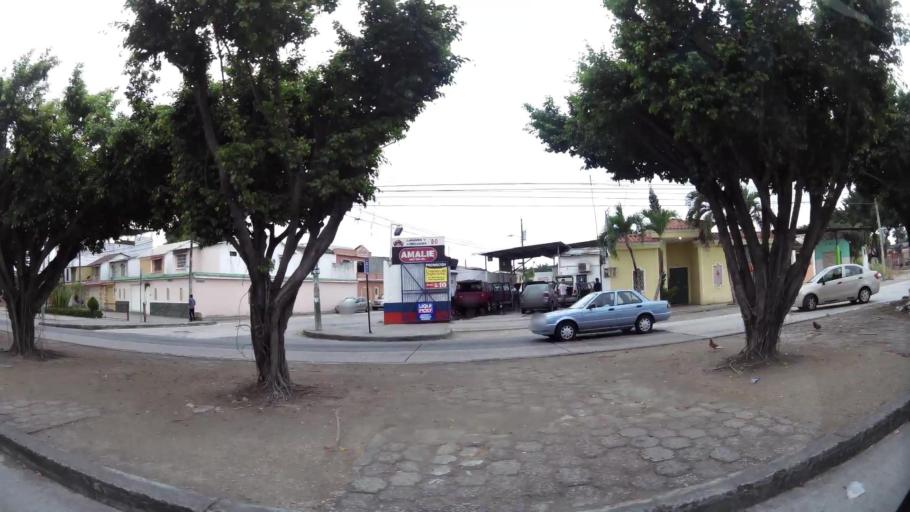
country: EC
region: Guayas
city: Eloy Alfaro
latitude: -2.1136
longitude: -79.8950
